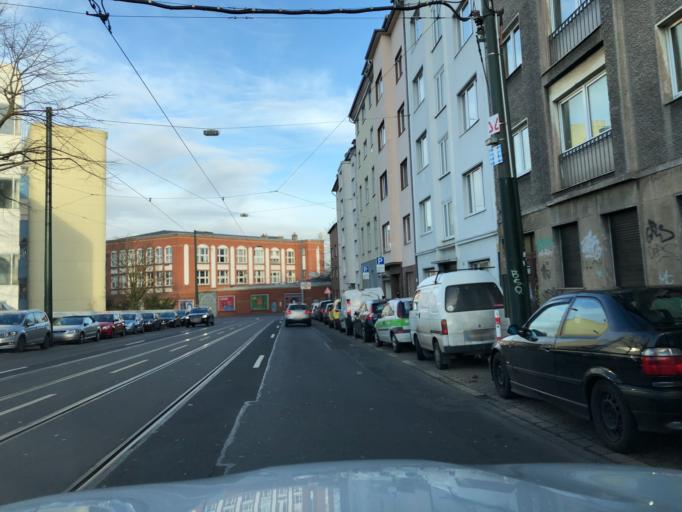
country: DE
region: North Rhine-Westphalia
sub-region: Regierungsbezirk Dusseldorf
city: Dusseldorf
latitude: 51.2227
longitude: 6.8016
